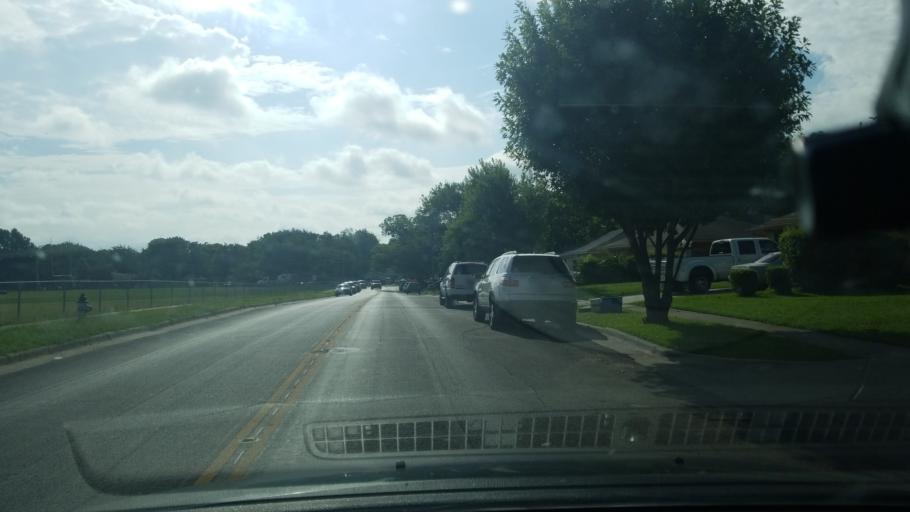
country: US
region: Texas
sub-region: Dallas County
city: Balch Springs
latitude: 32.7437
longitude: -96.6677
